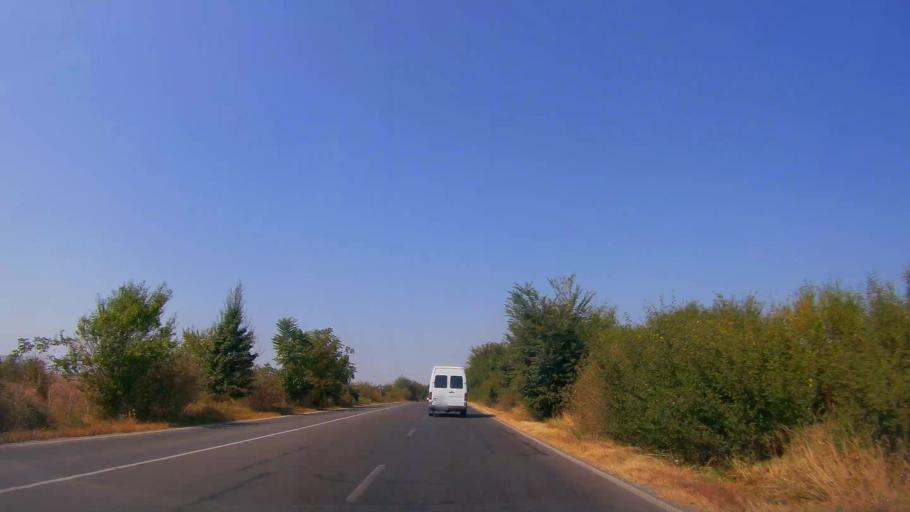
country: BG
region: Razgrad
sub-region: Obshtina Tsar Kaloyan
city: Tsar Kaloyan
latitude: 43.6286
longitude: 26.2061
